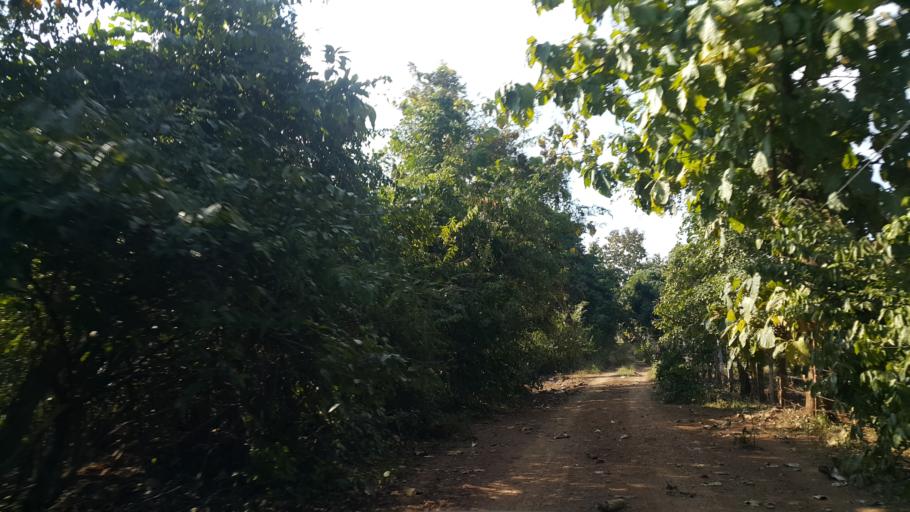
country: TH
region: Lamphun
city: Ban Thi
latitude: 18.5657
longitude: 99.1209
